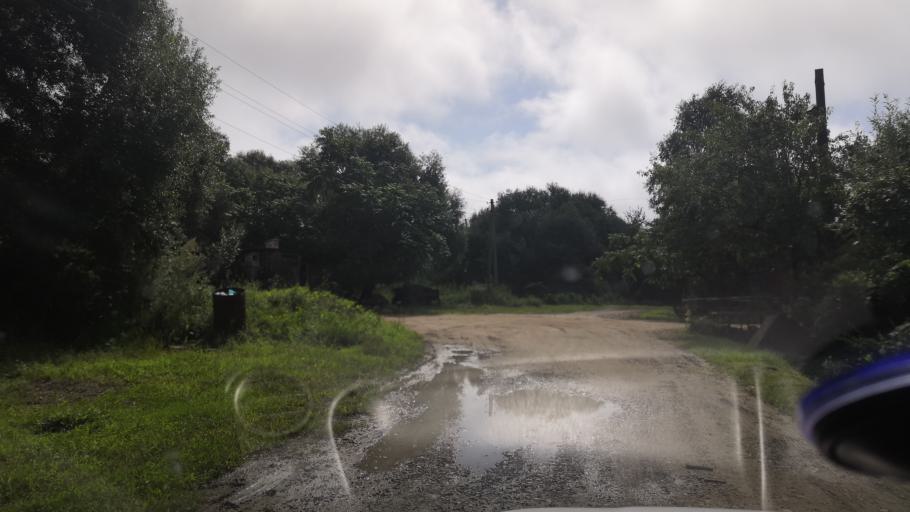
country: RU
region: Primorskiy
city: Dal'nerechensk
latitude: 45.9172
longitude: 133.7253
